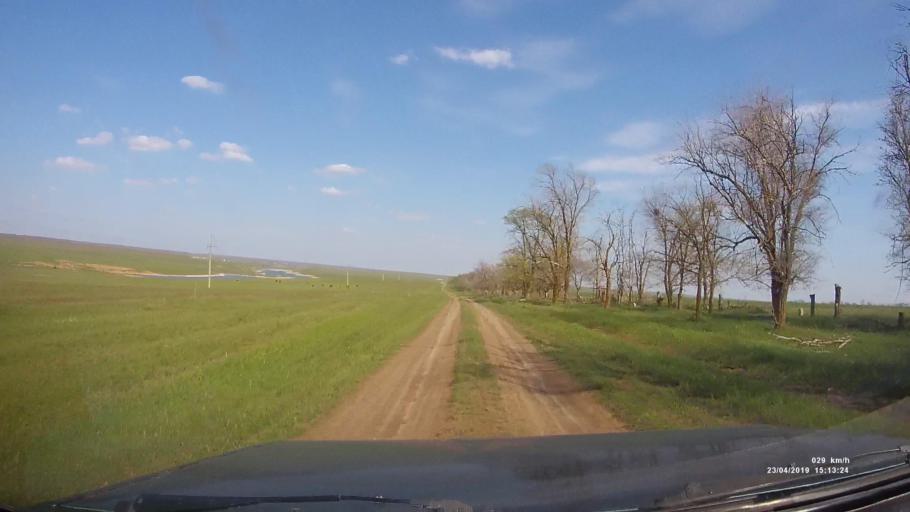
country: RU
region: Rostov
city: Remontnoye
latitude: 46.5397
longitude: 42.9556
